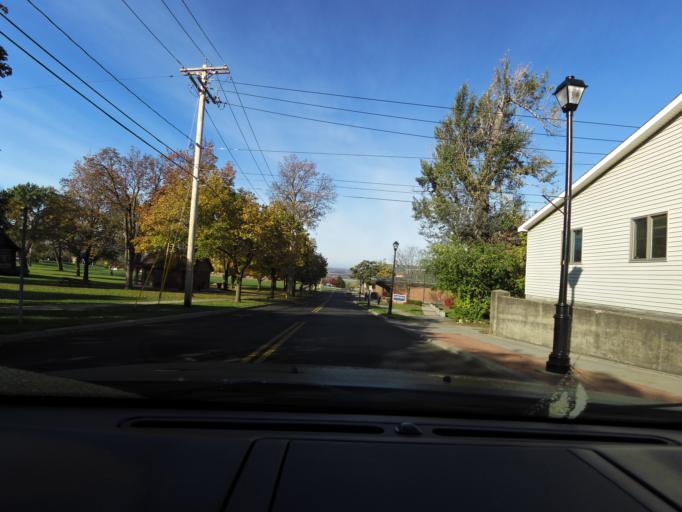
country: US
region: New York
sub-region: Livingston County
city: Geneseo
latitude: 42.7946
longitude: -77.8175
